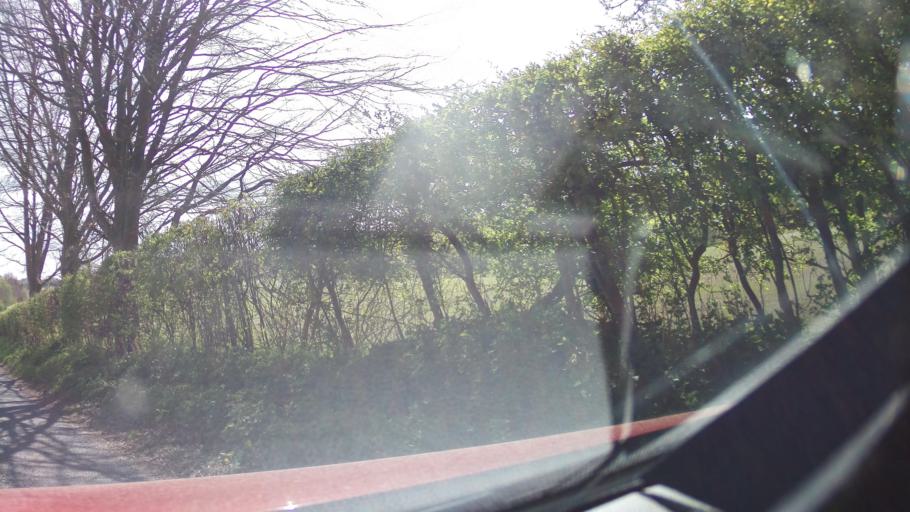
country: GB
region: England
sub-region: West Berkshire
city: Kintbury
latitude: 51.3430
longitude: -1.4707
